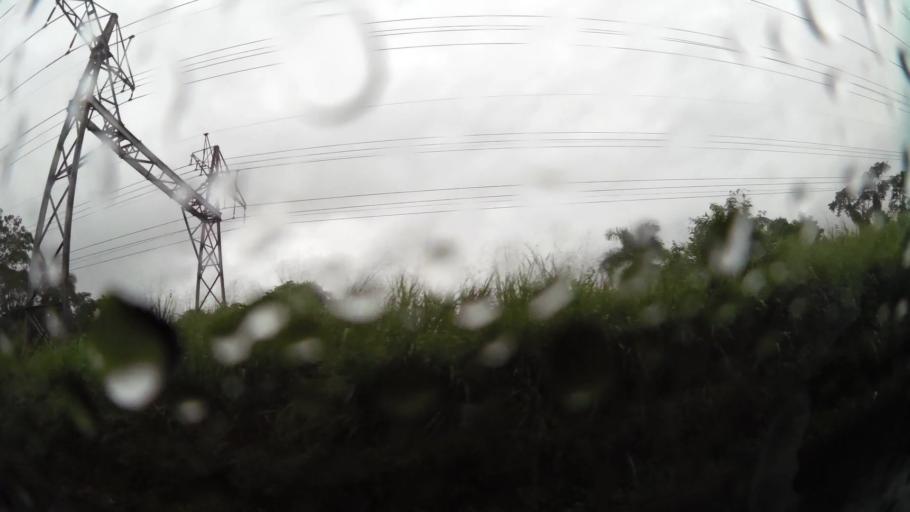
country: PA
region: Panama
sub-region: Distrito de Panama
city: Paraiso
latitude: 9.0160
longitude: -79.6057
